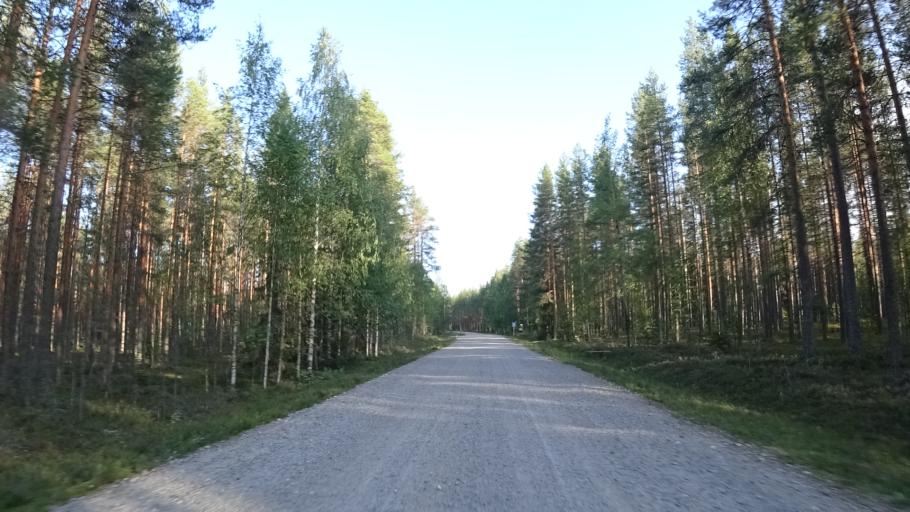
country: FI
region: North Karelia
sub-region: Joensuu
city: Ilomantsi
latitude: 63.1300
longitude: 30.7118
